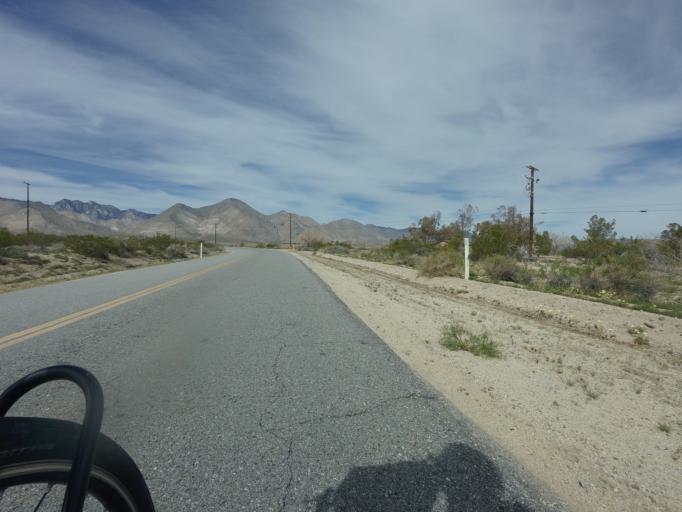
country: US
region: California
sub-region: Kern County
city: Inyokern
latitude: 35.7760
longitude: -117.8519
